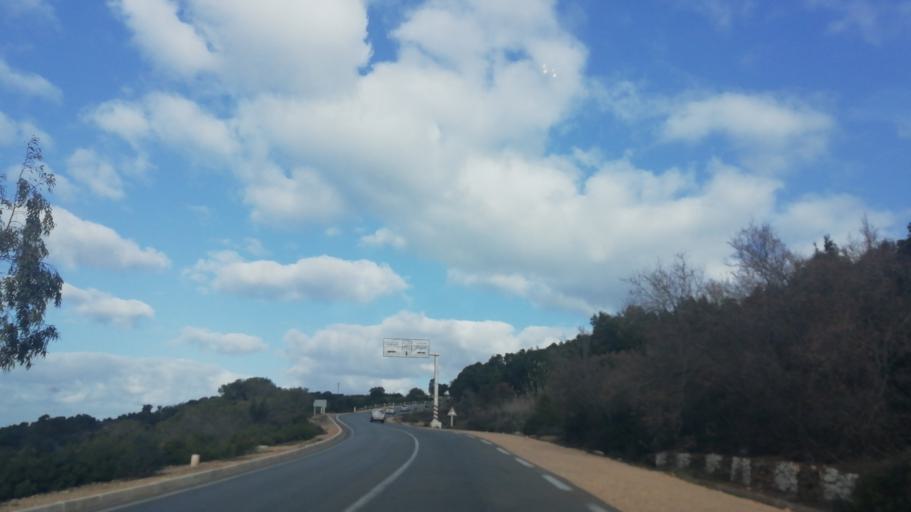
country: DZ
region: Relizane
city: Mazouna
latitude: 36.2418
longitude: 0.5384
